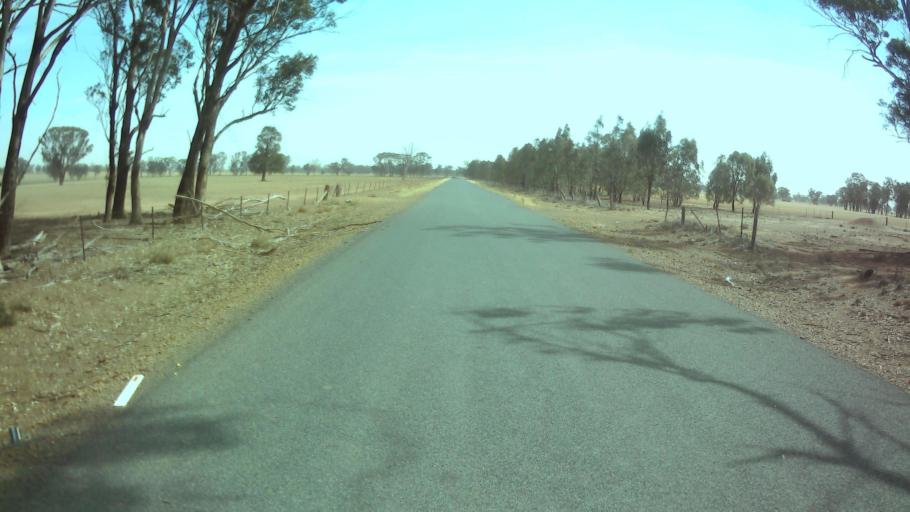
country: AU
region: New South Wales
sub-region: Weddin
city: Grenfell
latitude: -33.7151
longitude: 148.0009
